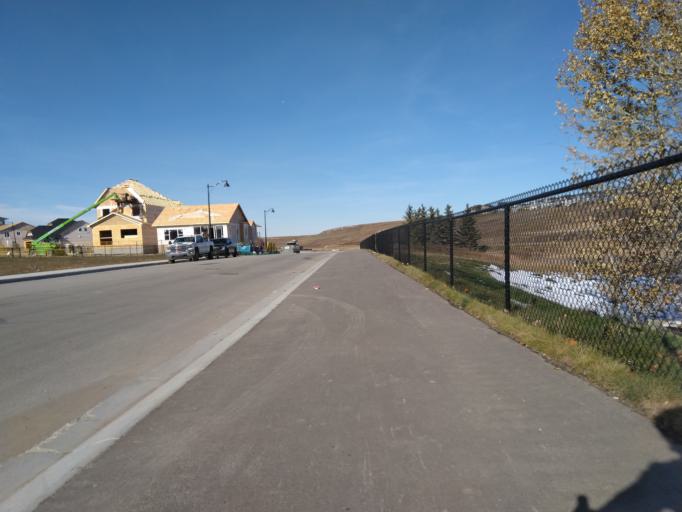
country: CA
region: Alberta
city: Calgary
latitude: 51.1766
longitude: -114.1297
